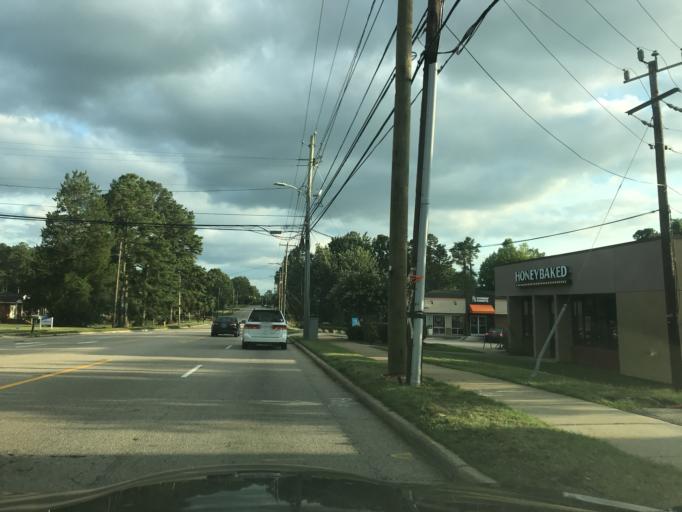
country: US
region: North Carolina
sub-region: Wake County
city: West Raleigh
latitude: 35.8537
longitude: -78.6425
